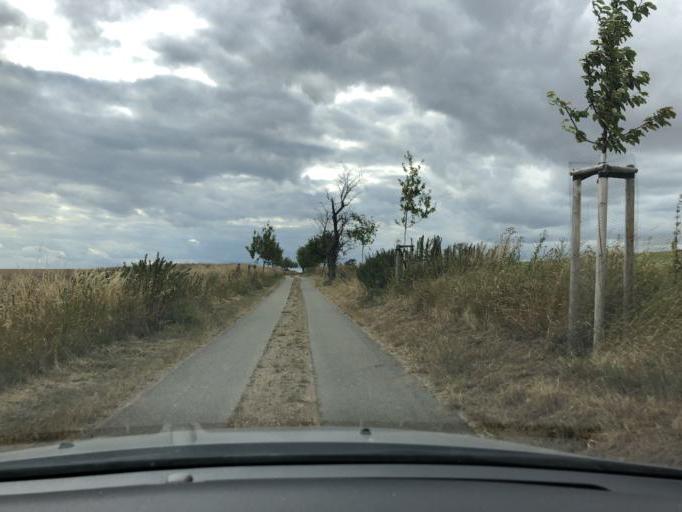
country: DE
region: Saxony
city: Geithain
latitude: 51.0206
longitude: 12.6496
